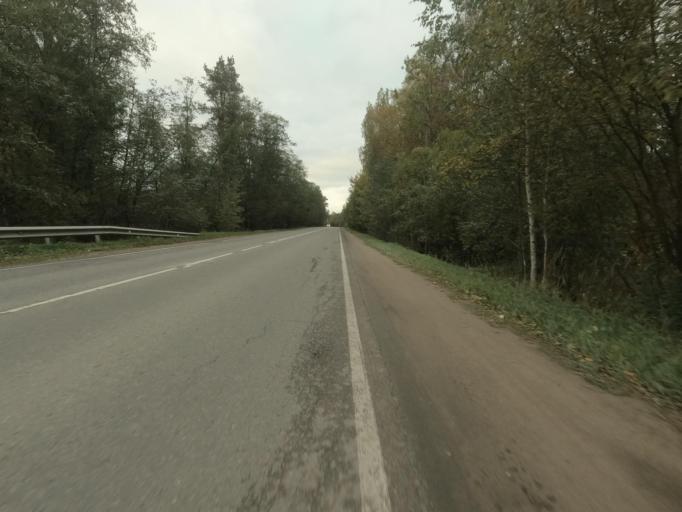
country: RU
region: Leningrad
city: Pavlovo
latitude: 59.7836
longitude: 30.9703
